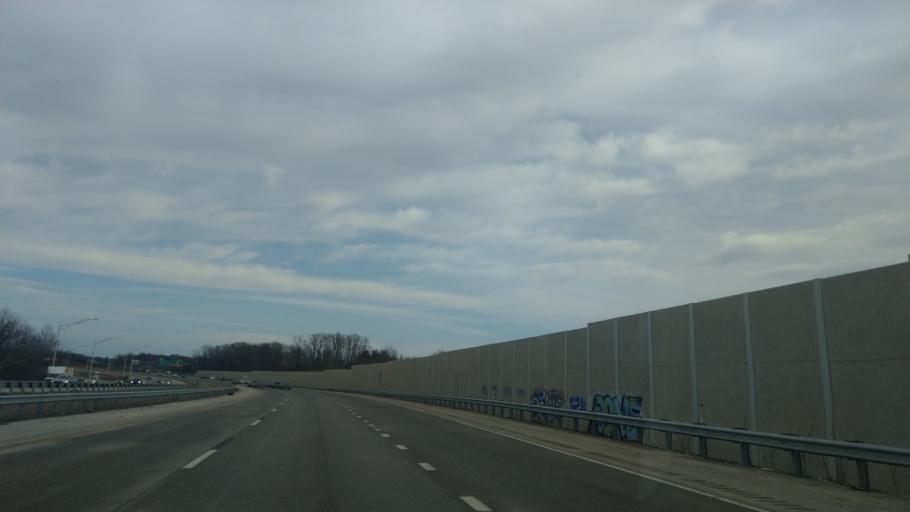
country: US
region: Pennsylvania
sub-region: Bucks County
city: Croydon
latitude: 40.1047
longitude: -74.8995
